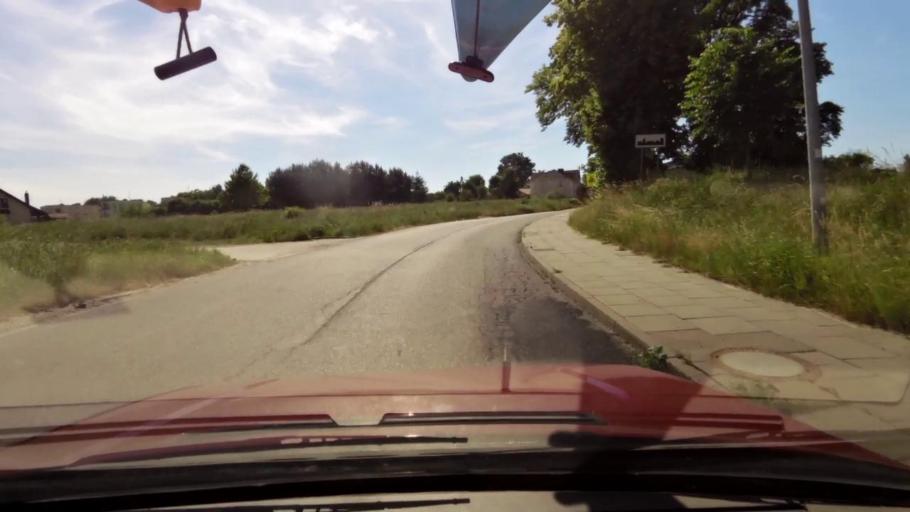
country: PL
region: Pomeranian Voivodeship
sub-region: Powiat slupski
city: Kobylnica
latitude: 54.3830
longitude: 16.9684
